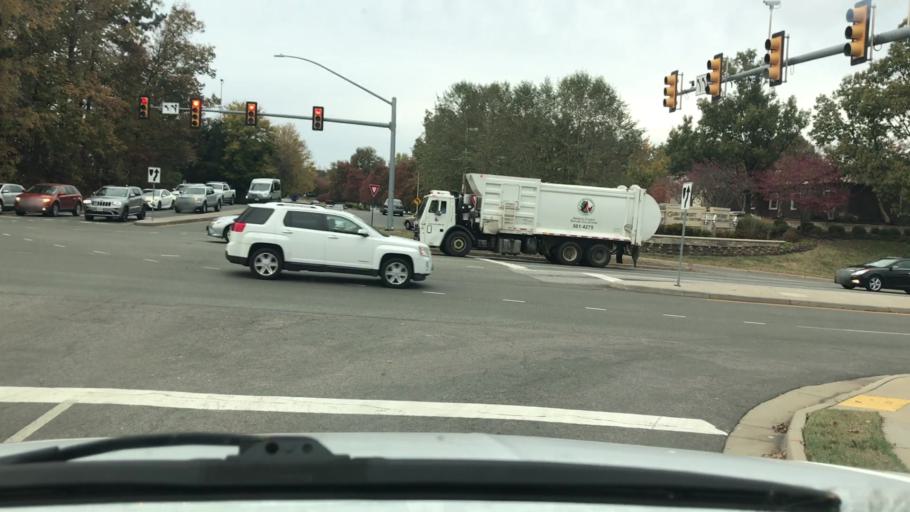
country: US
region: Virginia
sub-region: Henrico County
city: Tuckahoe
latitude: 37.6033
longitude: -77.5260
